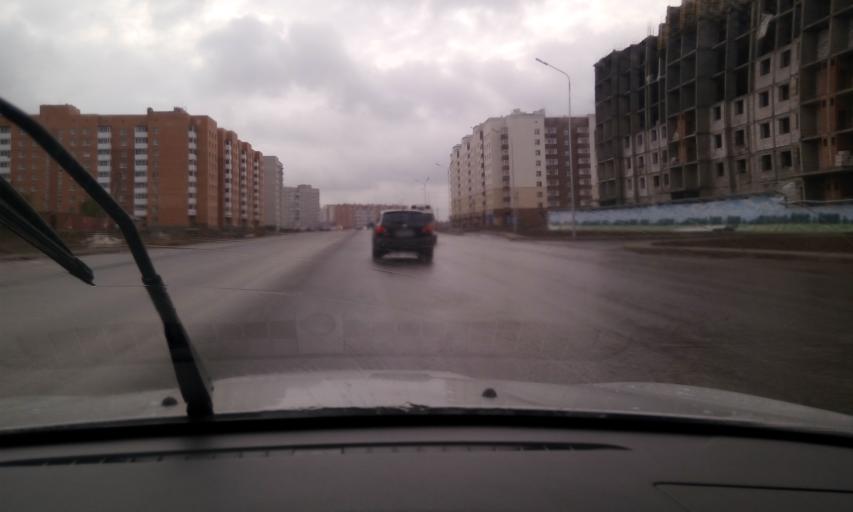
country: KZ
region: Astana Qalasy
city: Astana
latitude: 51.1282
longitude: 71.4979
